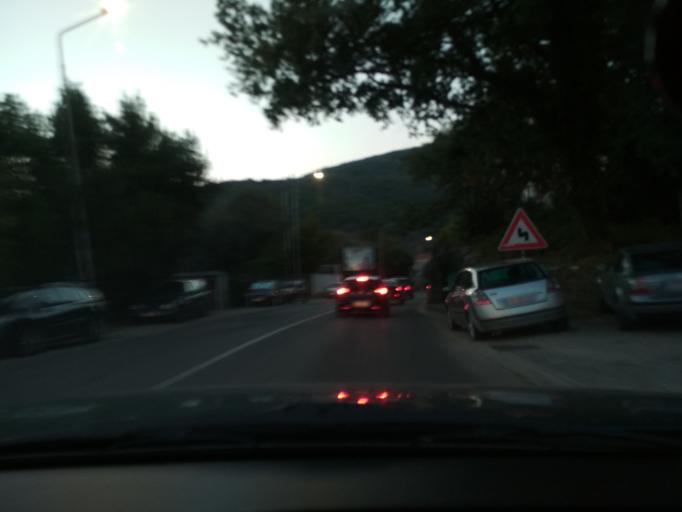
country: ME
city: Igalo
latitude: 42.4593
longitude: 18.5214
